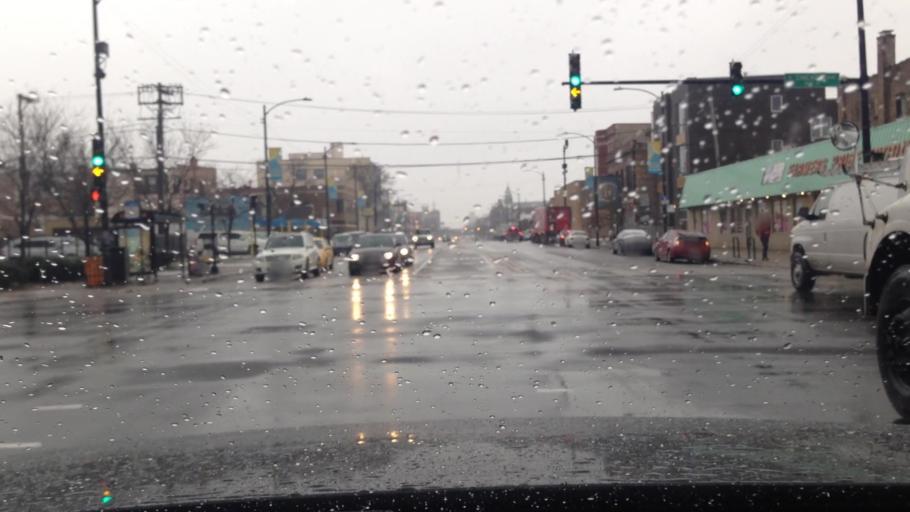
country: US
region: Illinois
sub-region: Cook County
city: Chicago
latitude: 41.8959
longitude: -87.6868
